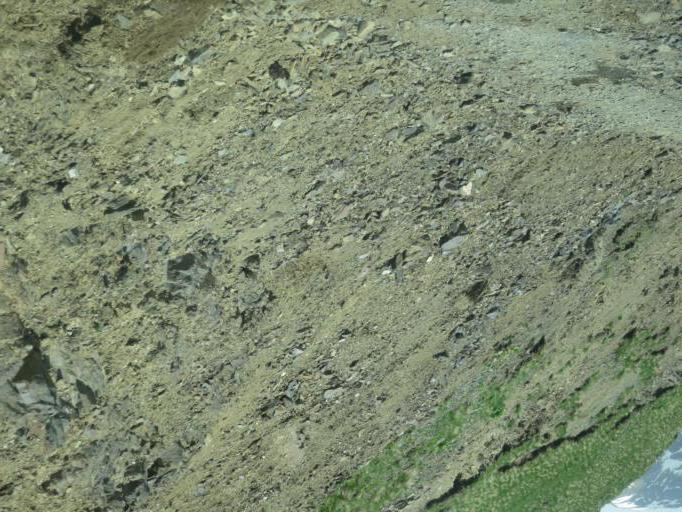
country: GE
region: Kakheti
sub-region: Telavi
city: Telavi
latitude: 42.2736
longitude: 45.4970
